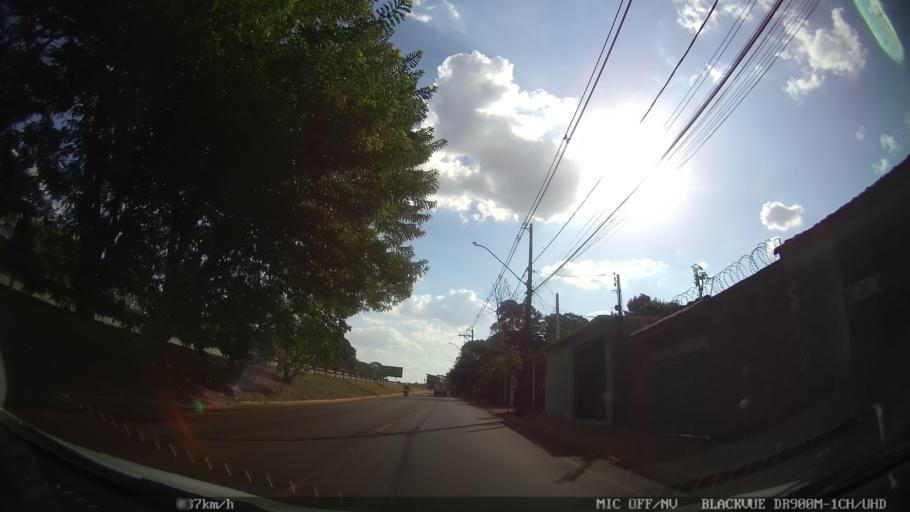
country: BR
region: Sao Paulo
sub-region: Ribeirao Preto
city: Ribeirao Preto
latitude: -21.1778
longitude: -47.8418
